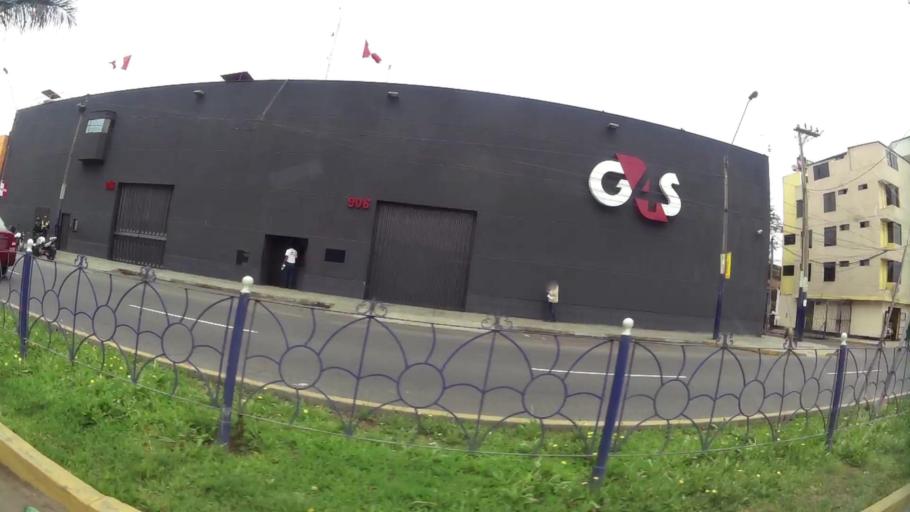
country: PE
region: Lima
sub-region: Lima
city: Surco
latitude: -12.1745
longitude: -77.0018
